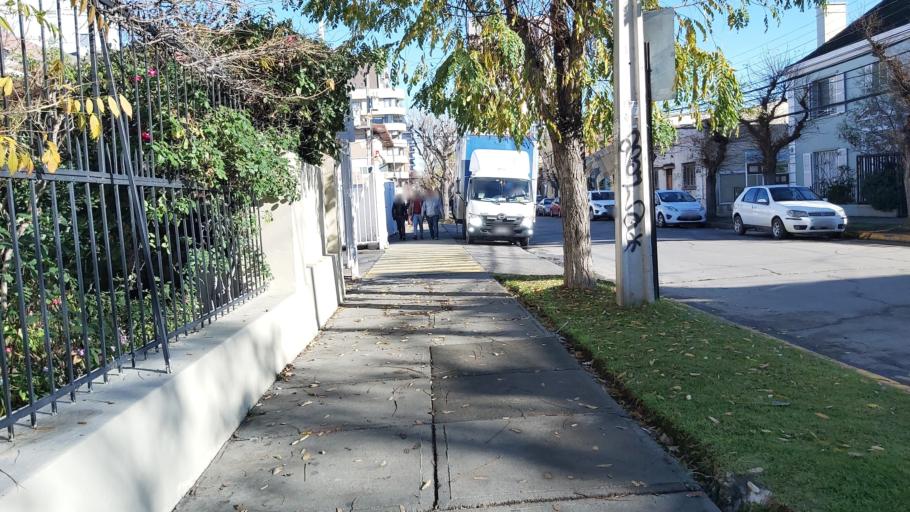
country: CL
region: Valparaiso
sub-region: Provincia de Valparaiso
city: Vina del Mar
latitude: -33.0179
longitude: -71.5468
